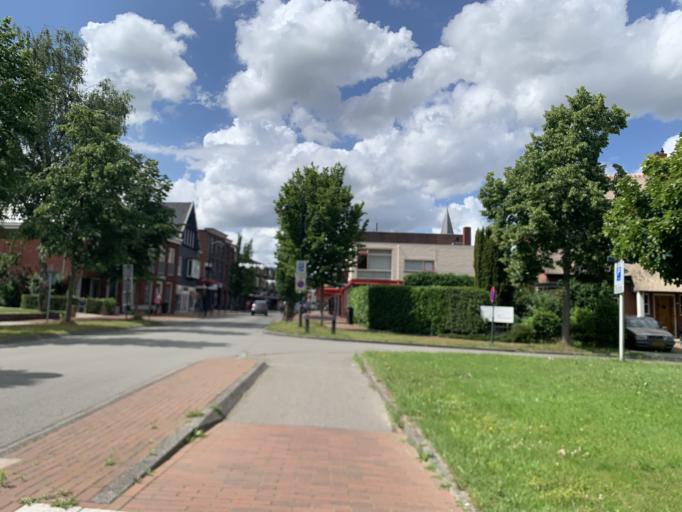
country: NL
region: Groningen
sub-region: Gemeente Haren
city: Haren
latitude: 53.1708
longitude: 6.6063
